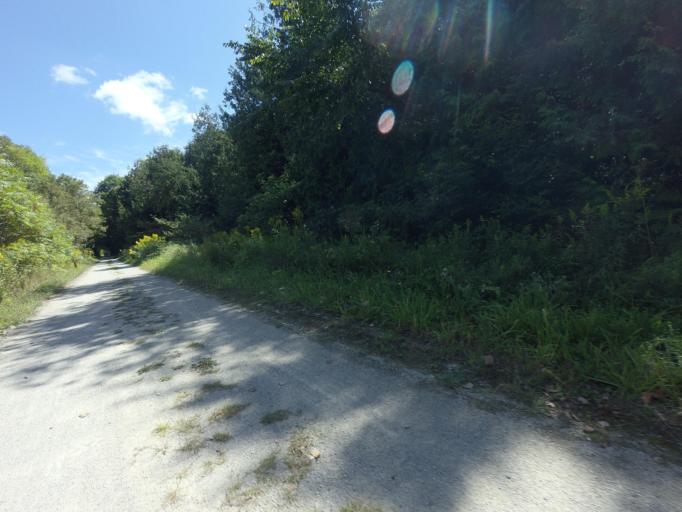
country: CA
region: Ontario
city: Orangeville
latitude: 43.7753
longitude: -80.1033
